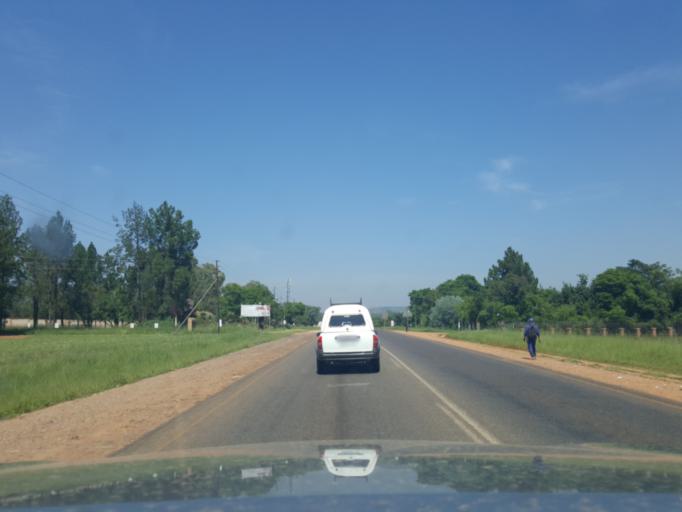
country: ZA
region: Gauteng
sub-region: City of Tshwane Metropolitan Municipality
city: Pretoria
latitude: -25.6760
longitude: 28.3305
